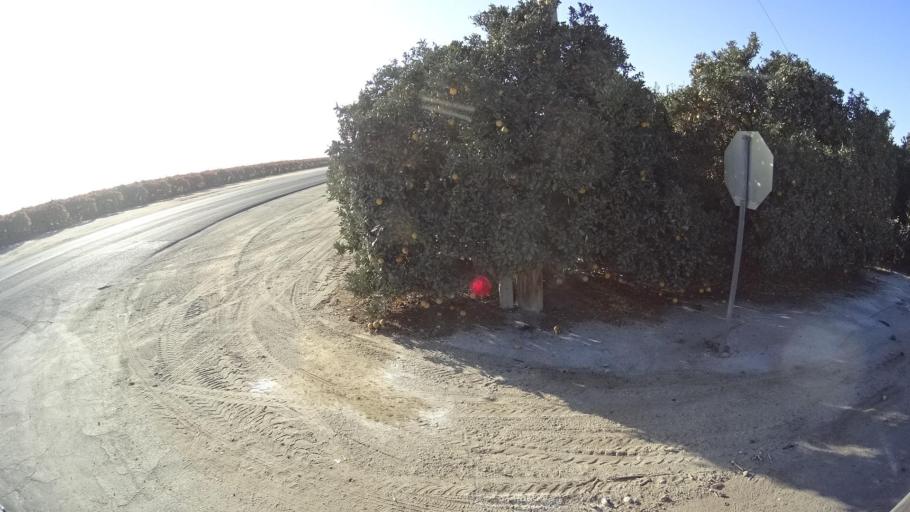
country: US
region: California
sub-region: Kern County
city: Delano
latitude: 35.7687
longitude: -119.1877
